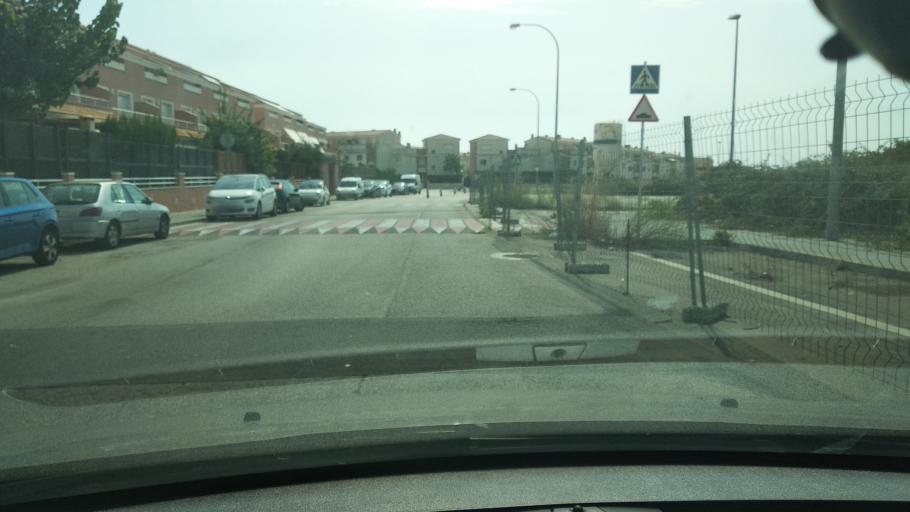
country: ES
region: Catalonia
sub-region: Provincia de Tarragona
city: El Vendrell
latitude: 41.2191
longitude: 1.5230
